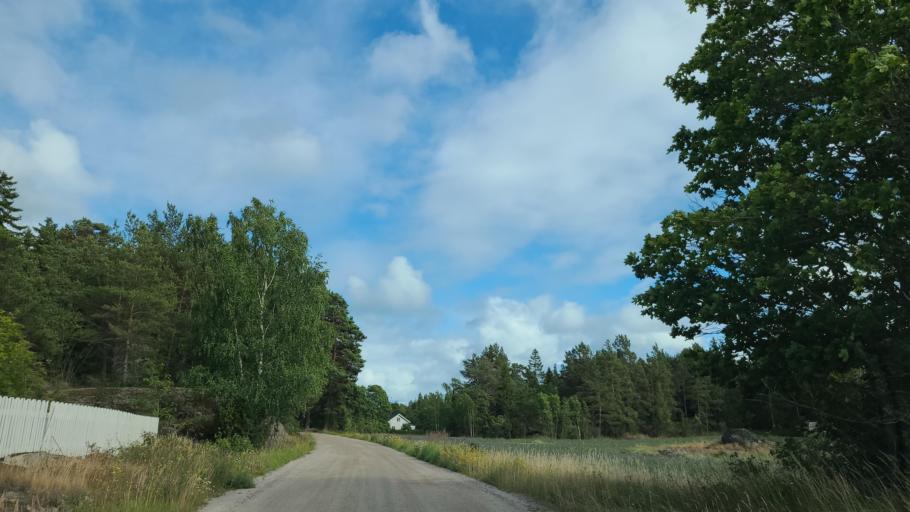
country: FI
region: Varsinais-Suomi
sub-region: Aboland-Turunmaa
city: Nagu
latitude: 60.1411
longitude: 21.7980
